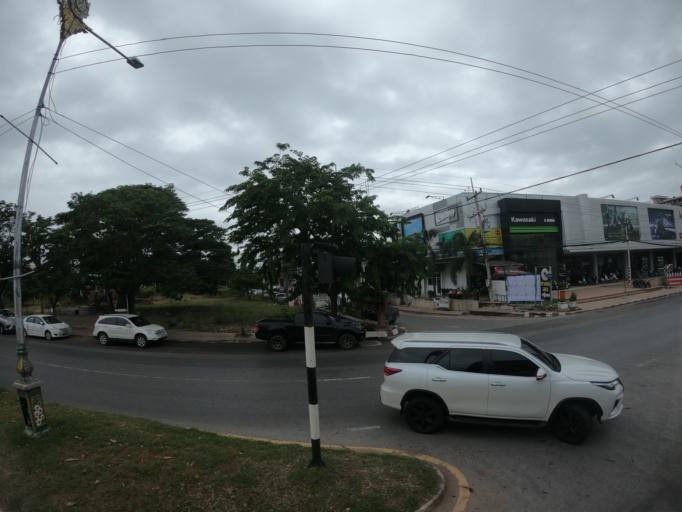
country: TH
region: Maha Sarakham
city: Maha Sarakham
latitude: 16.1790
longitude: 103.2981
